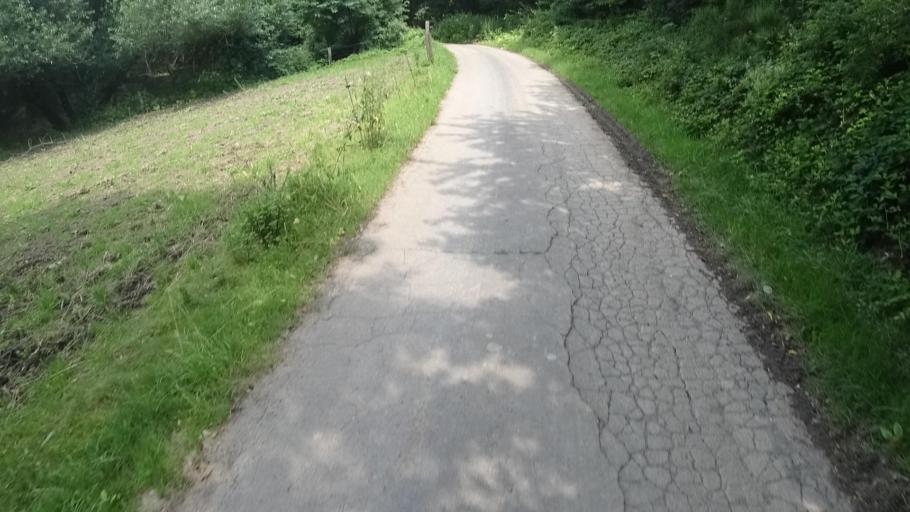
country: DE
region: Rheinland-Pfalz
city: Vettelschoss
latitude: 50.5932
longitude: 7.3598
